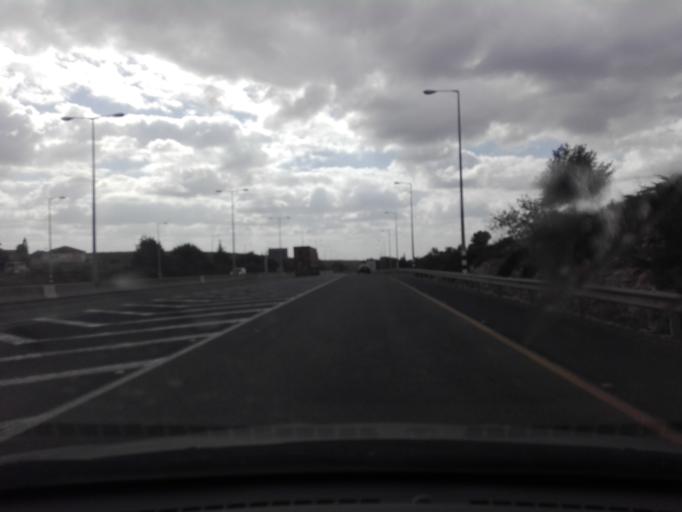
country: IL
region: Haifa
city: Daliyat el Karmil
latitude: 32.6321
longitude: 35.0632
